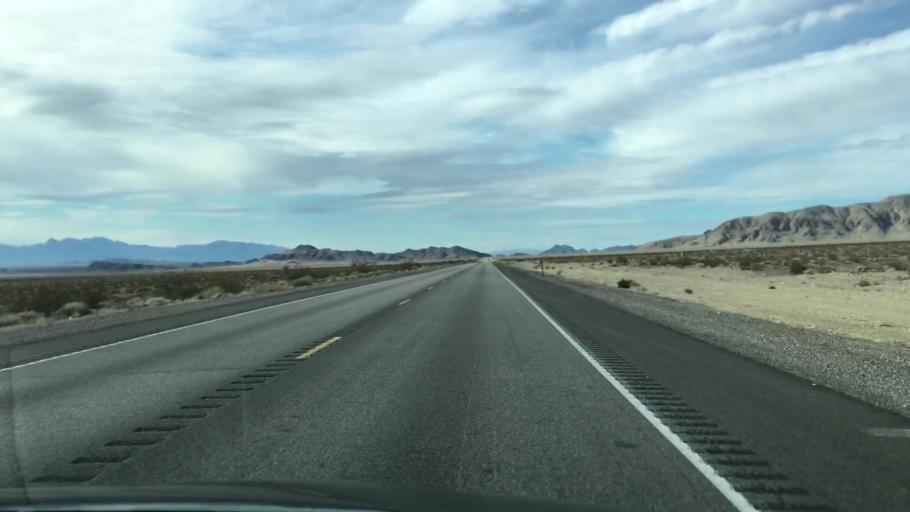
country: US
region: Nevada
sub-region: Nye County
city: Pahrump
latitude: 36.5688
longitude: -116.1510
